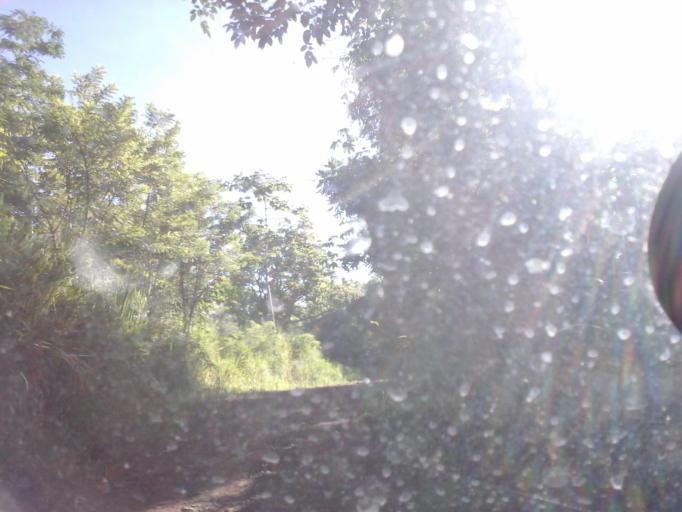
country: CO
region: Cesar
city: San Diego
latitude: 10.2709
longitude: -73.0908
